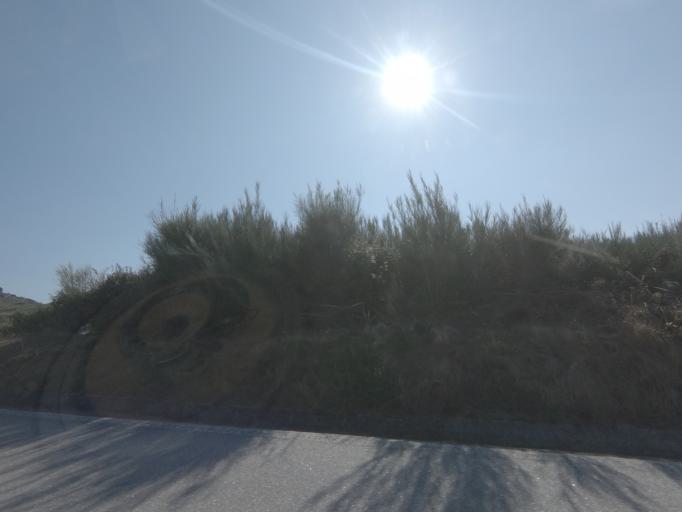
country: PT
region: Viseu
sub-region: Moimenta da Beira
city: Moimenta da Beira
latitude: 41.0328
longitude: -7.5680
